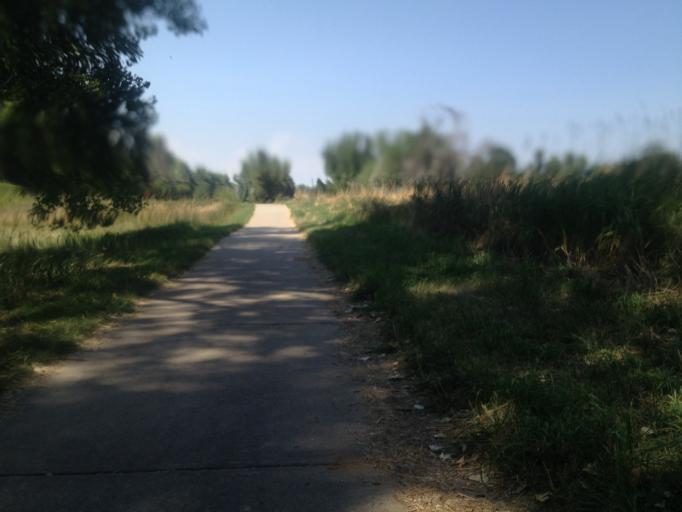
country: US
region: Colorado
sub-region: Boulder County
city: Louisville
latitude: 39.9944
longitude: -105.1377
